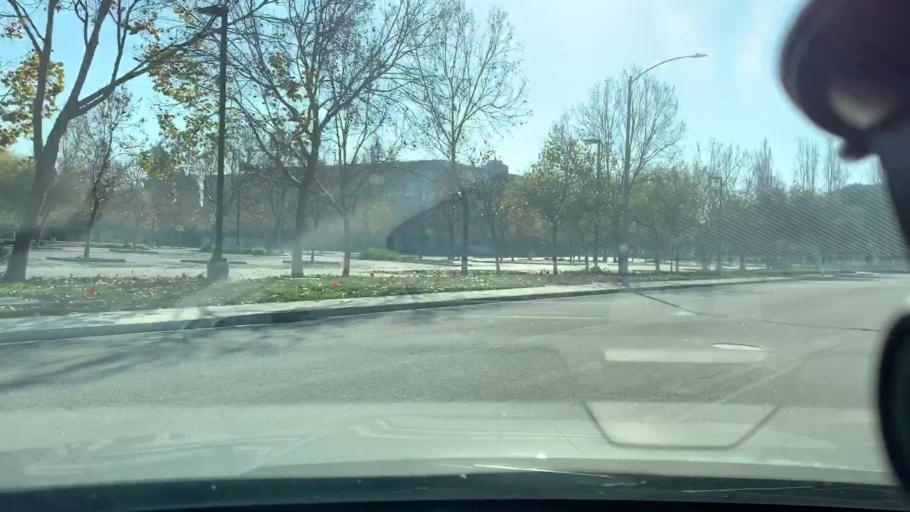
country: US
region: California
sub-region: Santa Clara County
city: Sunnyvale
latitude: 37.4129
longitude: -122.0134
